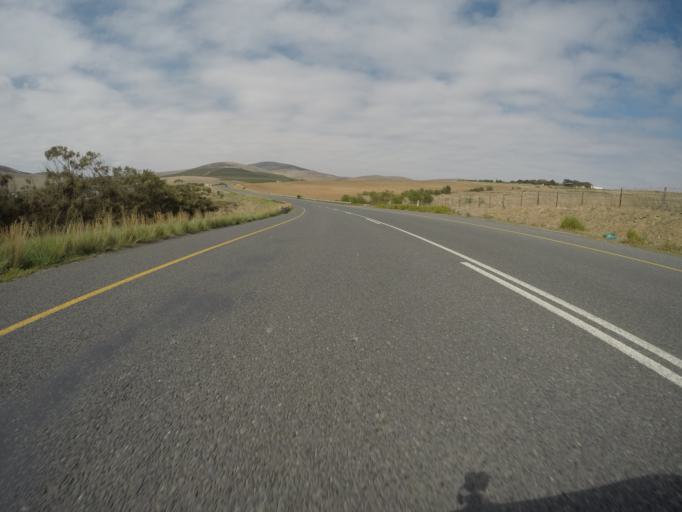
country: ZA
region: Western Cape
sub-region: City of Cape Town
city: Sunset Beach
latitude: -33.7887
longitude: 18.5765
